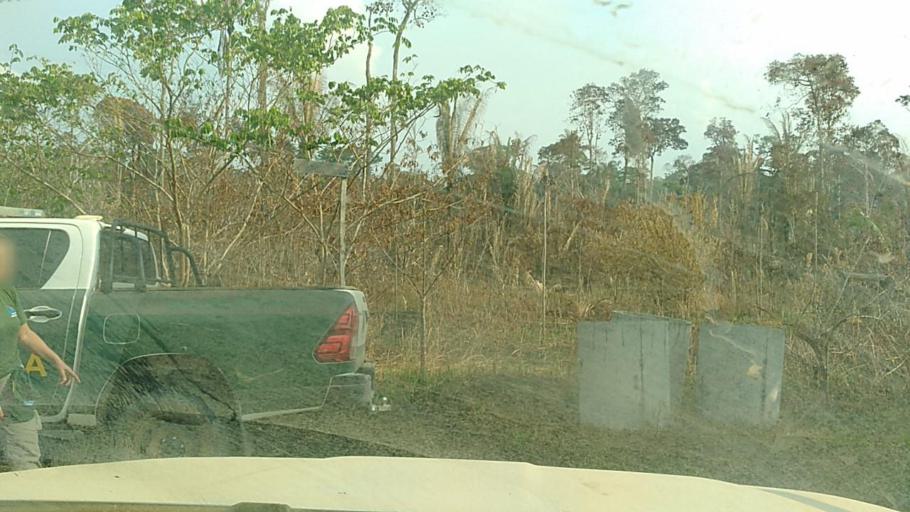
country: BR
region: Rondonia
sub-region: Porto Velho
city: Porto Velho
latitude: -8.5618
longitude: -64.0515
